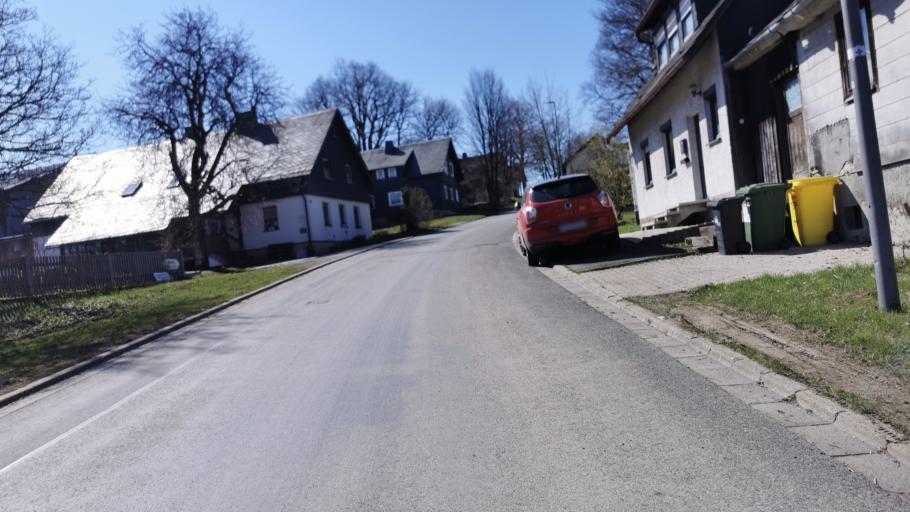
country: DE
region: Bavaria
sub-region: Upper Franconia
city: Teuschnitz
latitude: 50.4093
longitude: 11.3386
